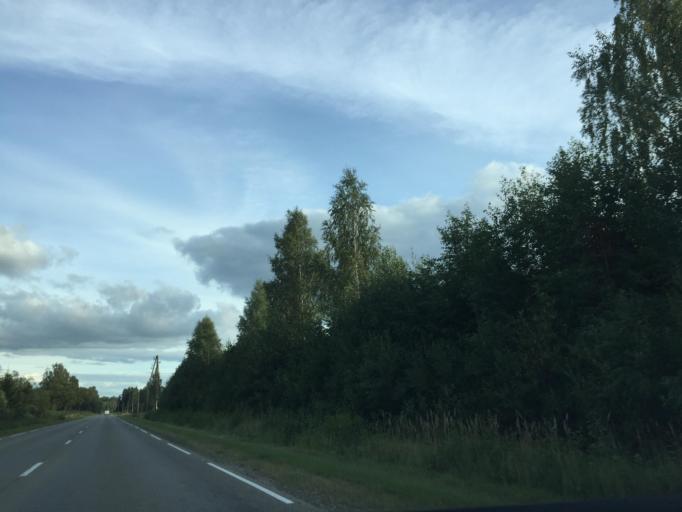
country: LV
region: Nereta
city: Nereta
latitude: 56.3030
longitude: 25.1053
